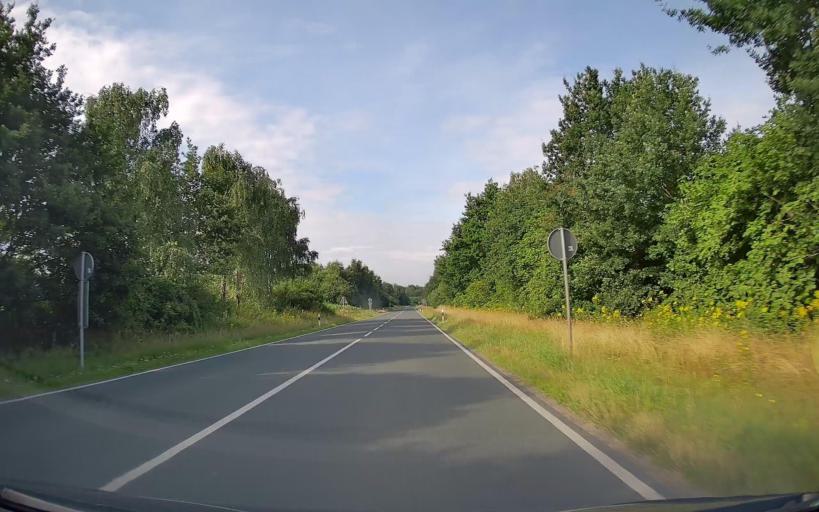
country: DE
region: Lower Saxony
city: Friesoythe
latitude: 53.0175
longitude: 7.8797
